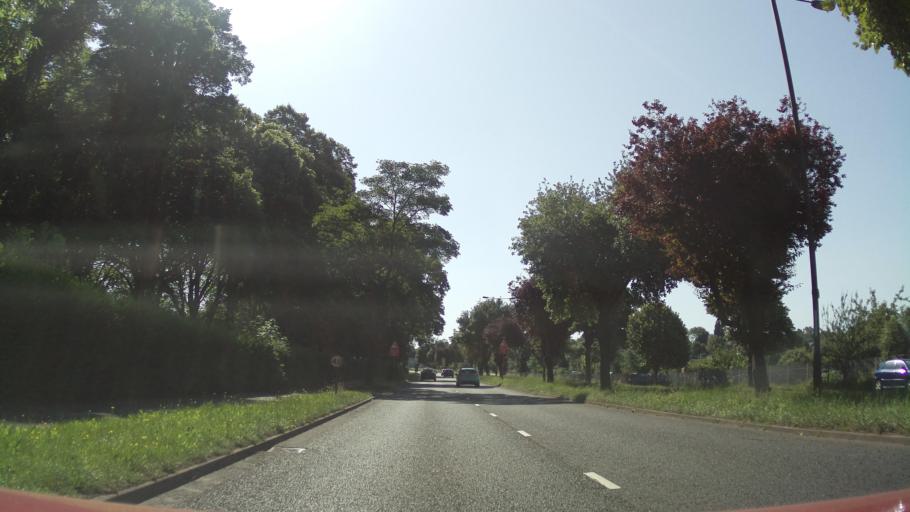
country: GB
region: England
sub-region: Derby
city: Derby
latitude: 52.9032
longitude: -1.4947
